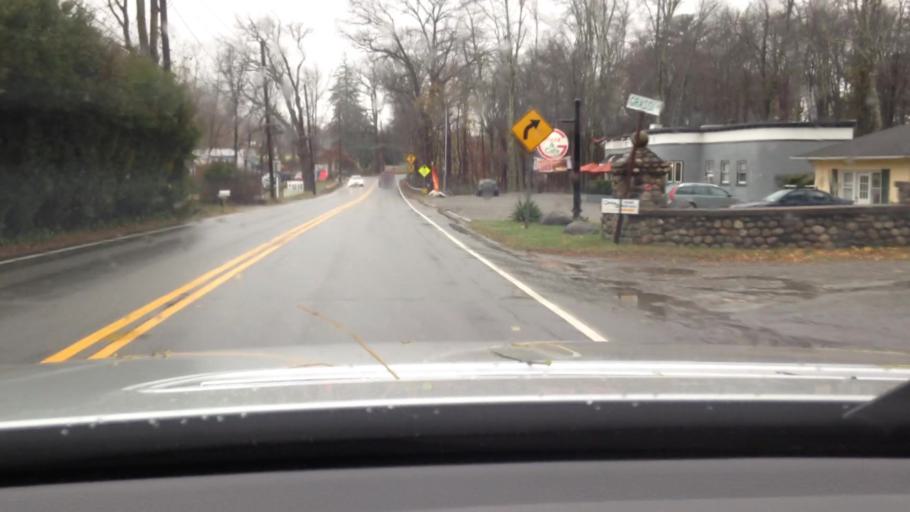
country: US
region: New York
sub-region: Orange County
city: West Point
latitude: 41.3838
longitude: -73.9360
